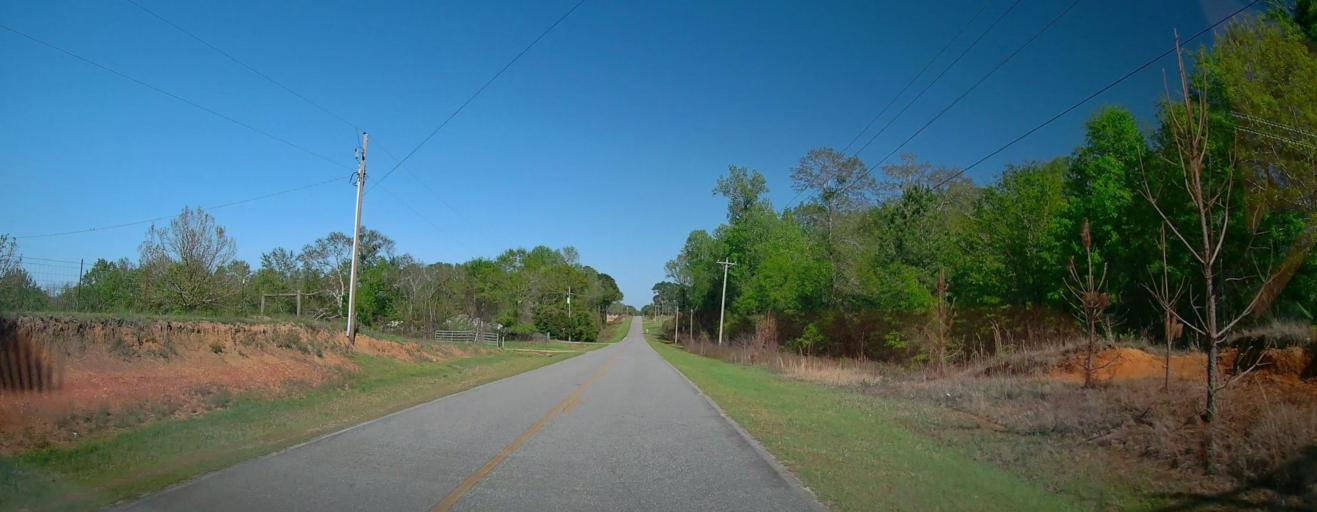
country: US
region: Georgia
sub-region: Pulaski County
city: Hawkinsville
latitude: 32.2478
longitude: -83.4936
